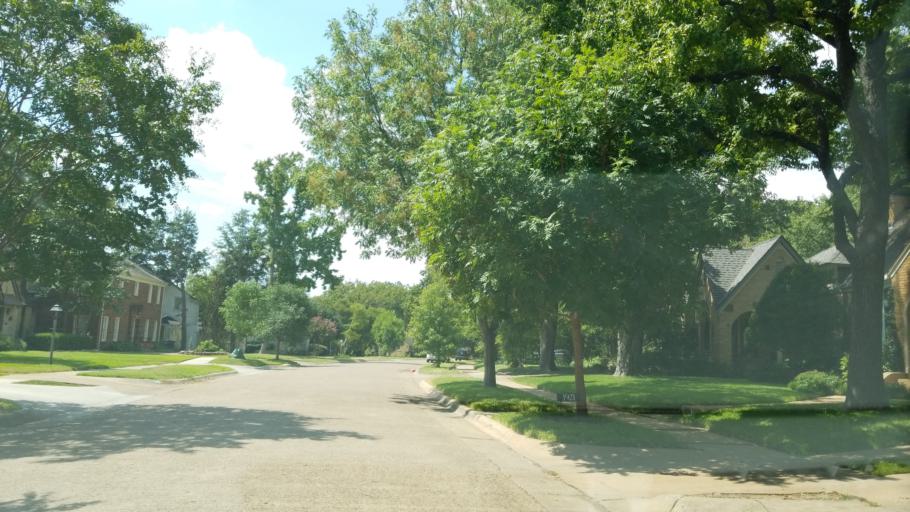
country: US
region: Texas
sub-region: Dallas County
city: Cockrell Hill
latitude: 32.7584
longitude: -96.8531
